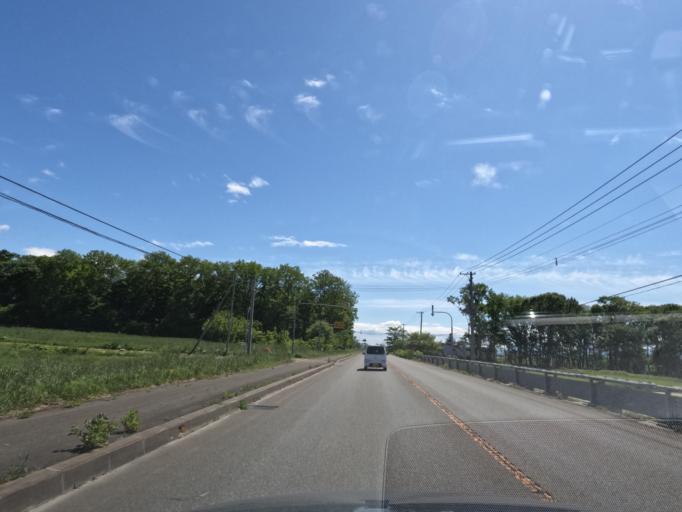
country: JP
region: Hokkaido
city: Iwamizawa
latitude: 43.0510
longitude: 141.7283
